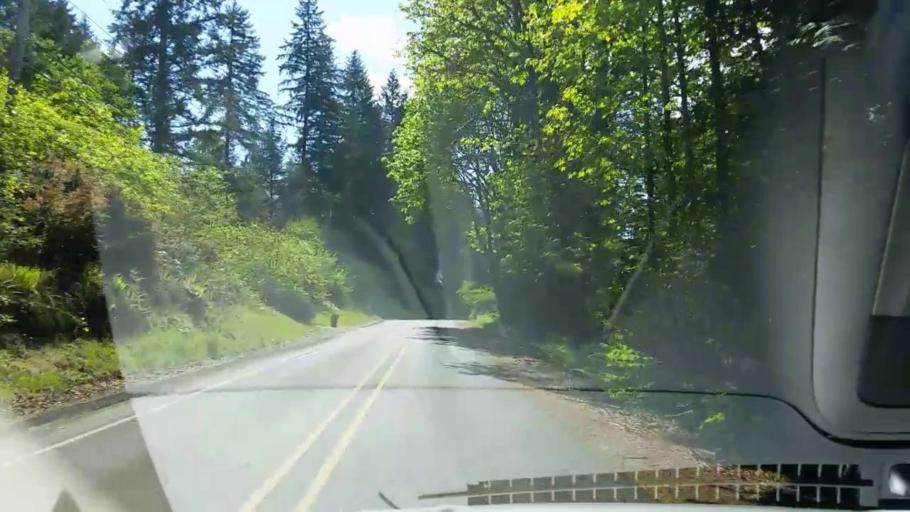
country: US
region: Washington
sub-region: Pierce County
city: Key Center
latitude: 47.3430
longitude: -122.7417
